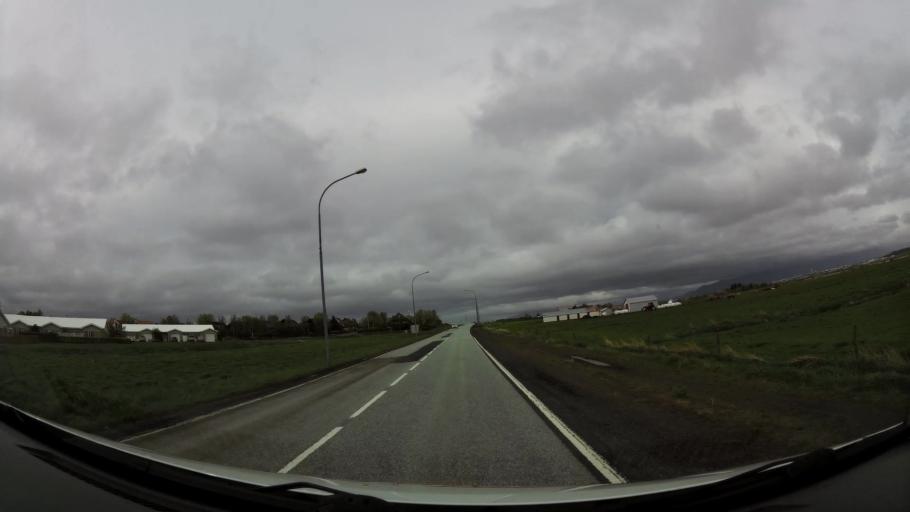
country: IS
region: Capital Region
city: Alftanes
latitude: 64.1050
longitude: -22.0097
